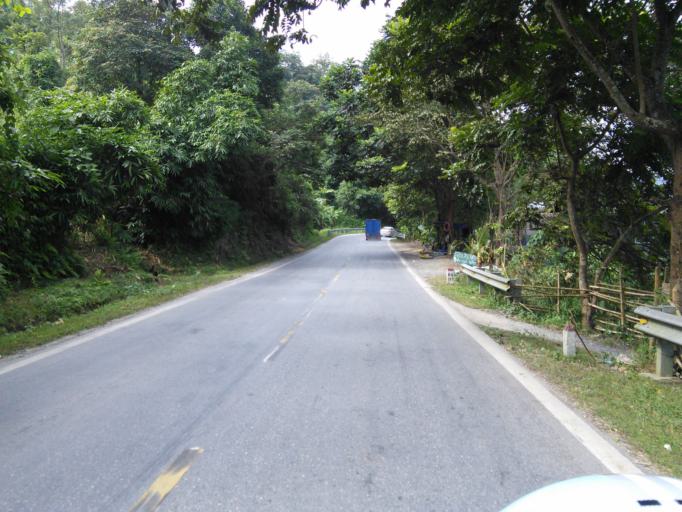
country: VN
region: Lao Cai
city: Lao Cai
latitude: 22.4453
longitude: 103.9379
